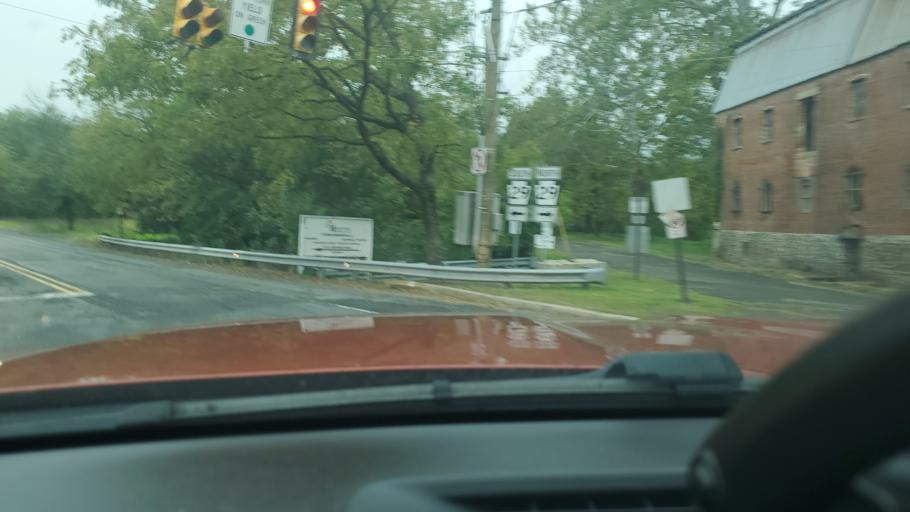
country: US
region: Pennsylvania
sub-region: Montgomery County
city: Woxall
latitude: 40.3244
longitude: -75.4788
